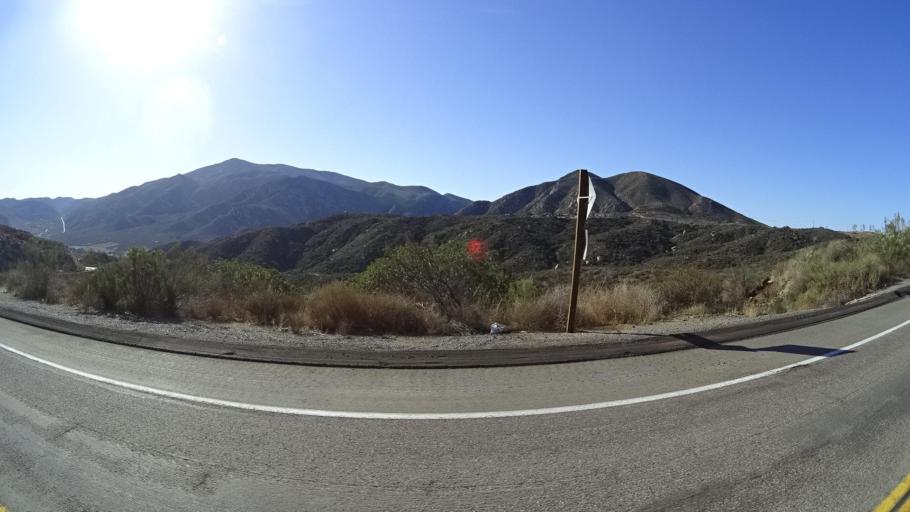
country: MX
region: Baja California
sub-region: Tecate
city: Lomas de Santa Anita
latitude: 32.6178
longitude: -116.7303
